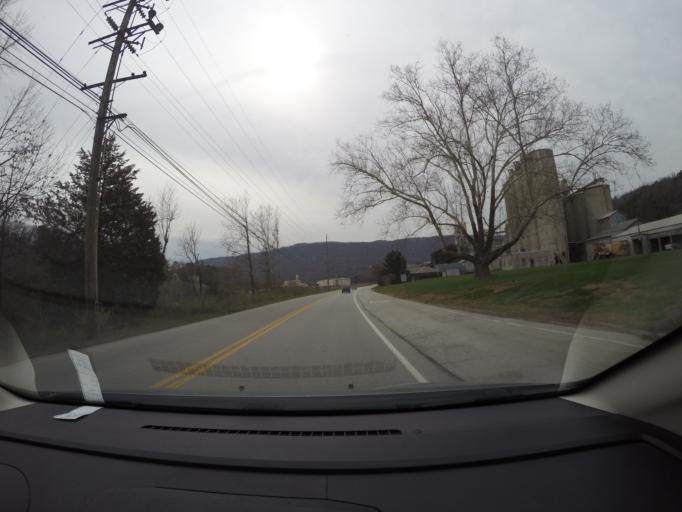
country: US
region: Tennessee
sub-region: Hamilton County
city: Signal Mountain
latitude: 35.1015
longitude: -85.3395
